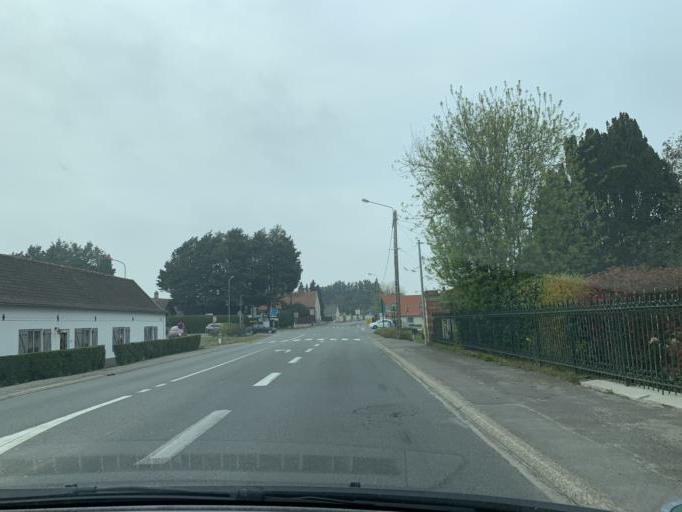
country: FR
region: Nord-Pas-de-Calais
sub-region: Departement du Pas-de-Calais
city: Montreuil
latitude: 50.4039
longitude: 1.7256
